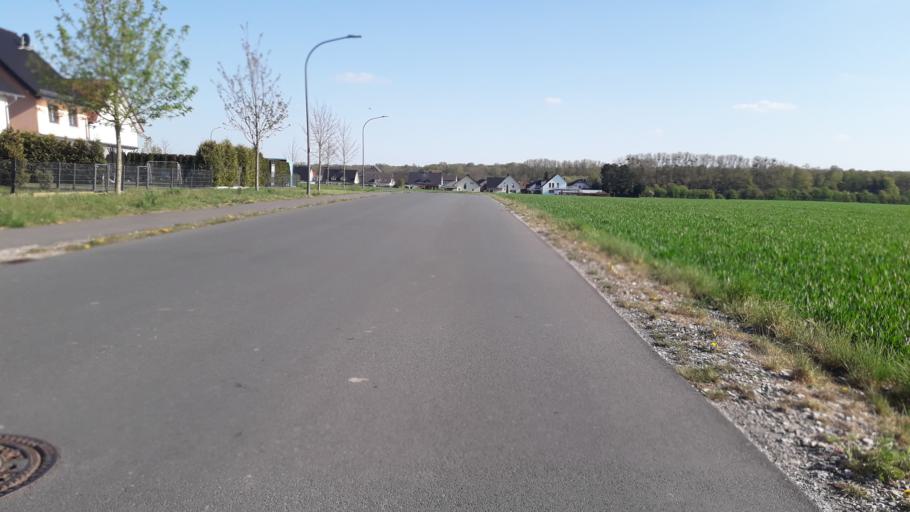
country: DE
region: North Rhine-Westphalia
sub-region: Regierungsbezirk Detmold
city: Paderborn
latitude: 51.6876
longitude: 8.6809
